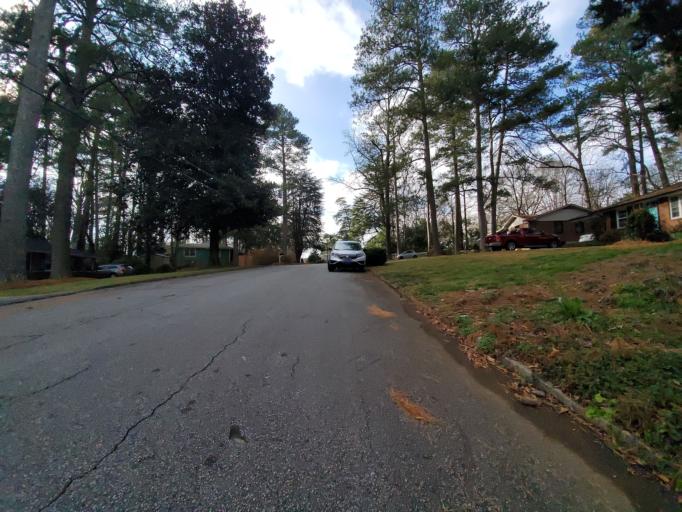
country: US
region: Georgia
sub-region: DeKalb County
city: Scottdale
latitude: 33.8040
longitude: -84.2803
